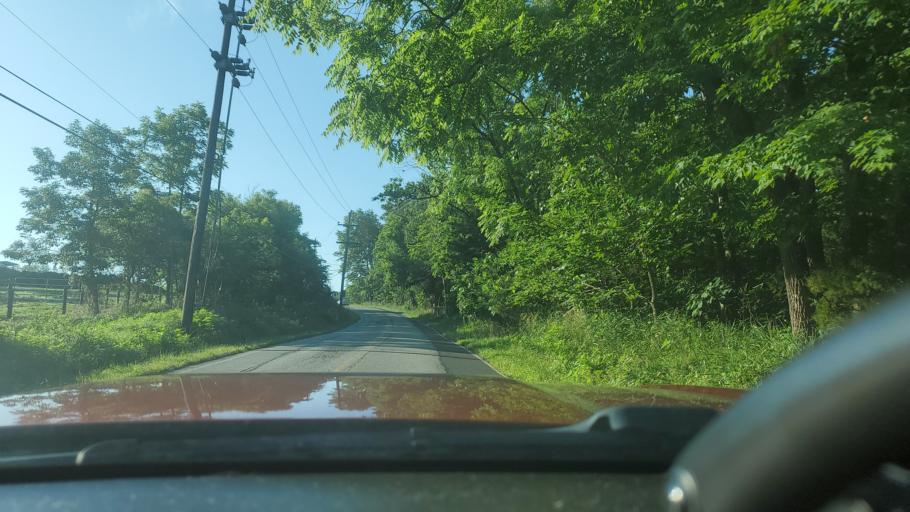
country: US
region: Pennsylvania
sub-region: Montgomery County
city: Woxall
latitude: 40.3215
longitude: -75.4717
